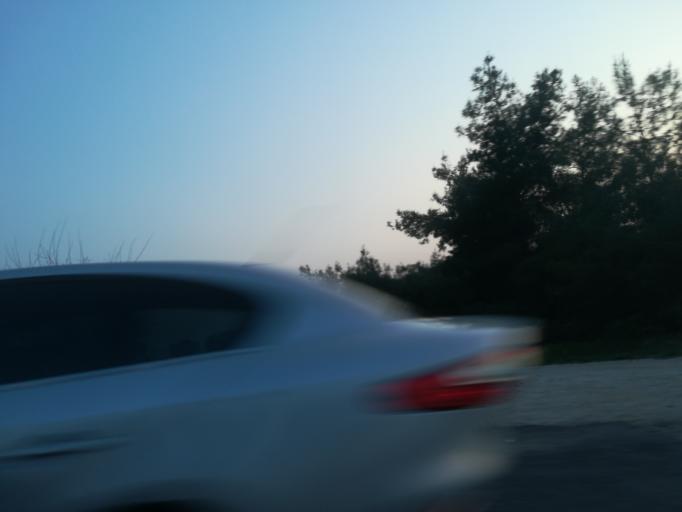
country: TR
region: Adana
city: Adana
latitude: 37.0734
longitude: 35.4056
